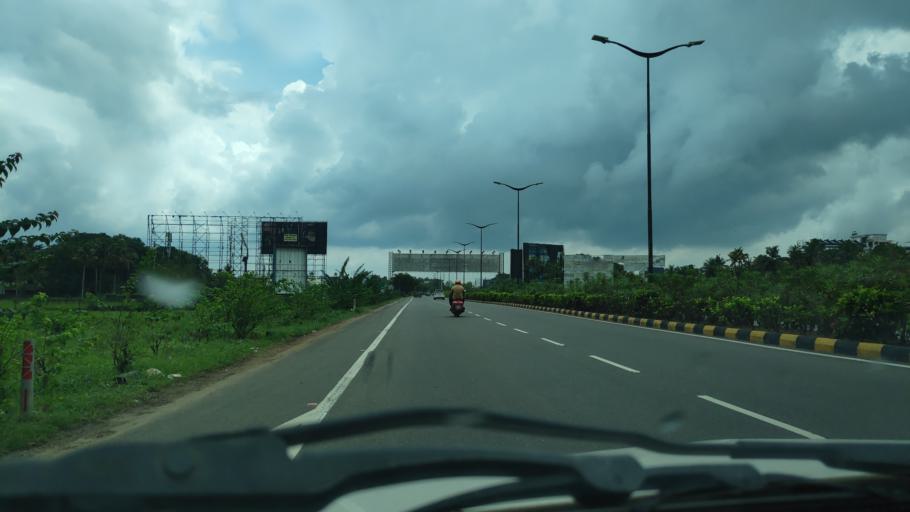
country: IN
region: Kerala
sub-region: Ernakulam
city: Aluva
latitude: 10.1501
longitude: 76.3616
